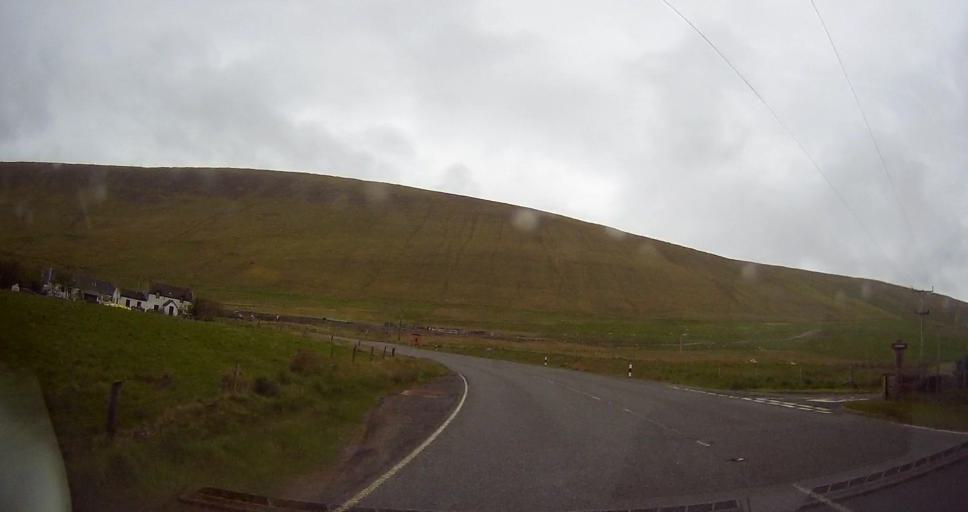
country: GB
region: Scotland
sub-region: Shetland Islands
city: Lerwick
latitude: 60.2541
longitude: -1.2926
